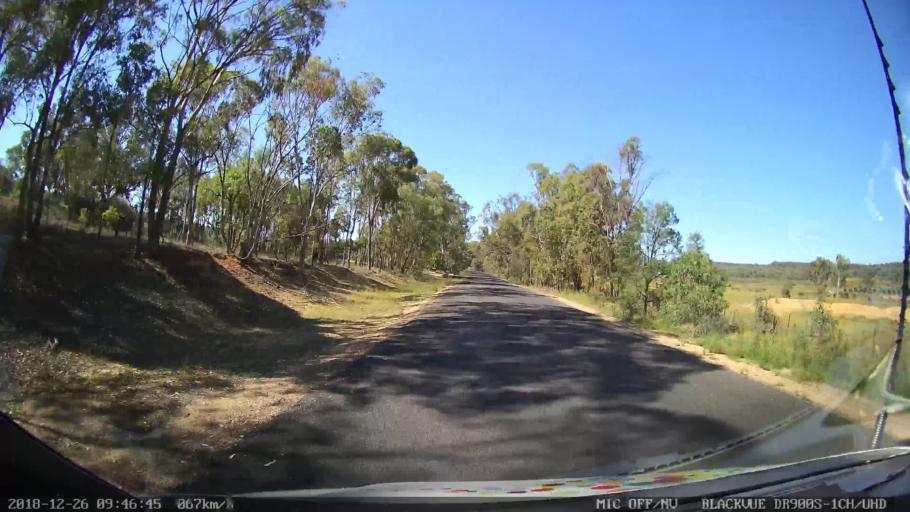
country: AU
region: New South Wales
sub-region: Mid-Western Regional
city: Kandos
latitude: -32.9728
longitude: 150.1047
